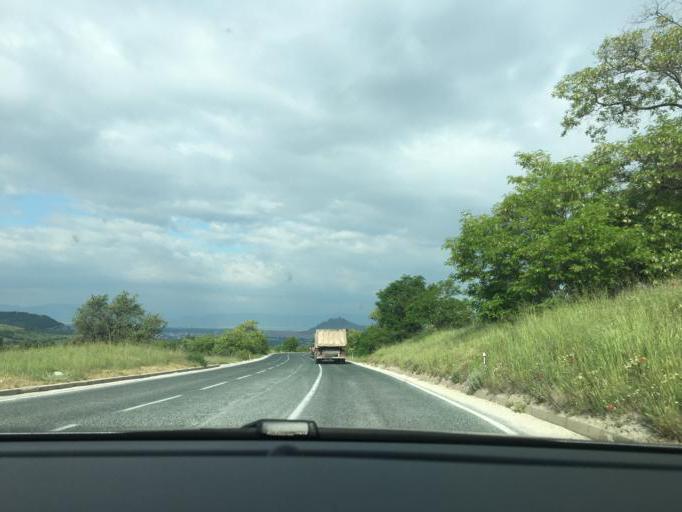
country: MK
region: Prilep
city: Prilep
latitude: 41.3694
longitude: 21.6327
